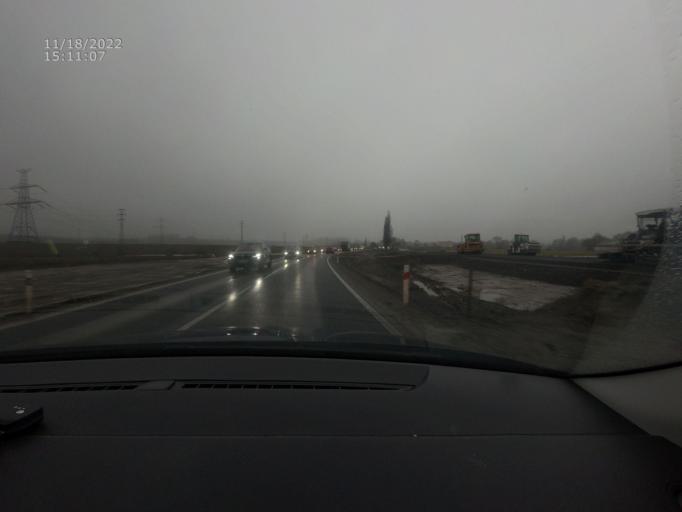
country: CZ
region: Jihocesky
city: Mirovice
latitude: 49.5323
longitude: 14.0780
